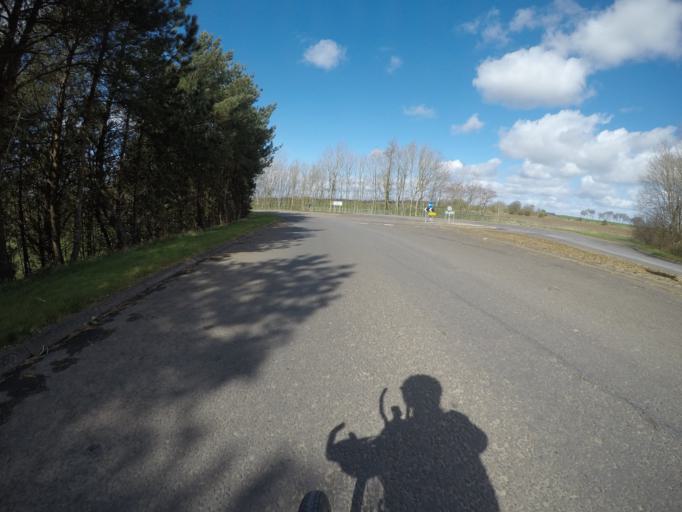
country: GB
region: Scotland
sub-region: North Ayrshire
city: Springside
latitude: 55.6148
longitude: -4.6050
